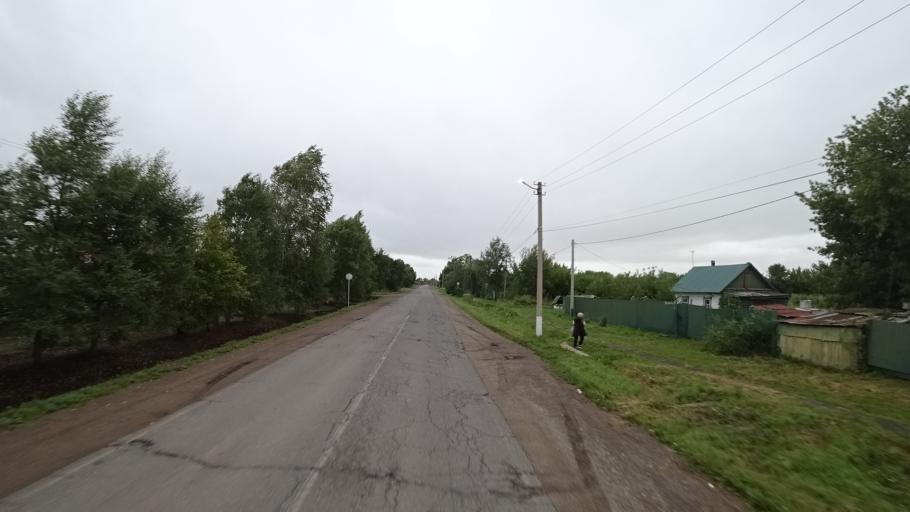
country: RU
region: Primorskiy
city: Chernigovka
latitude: 44.3443
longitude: 132.5474
